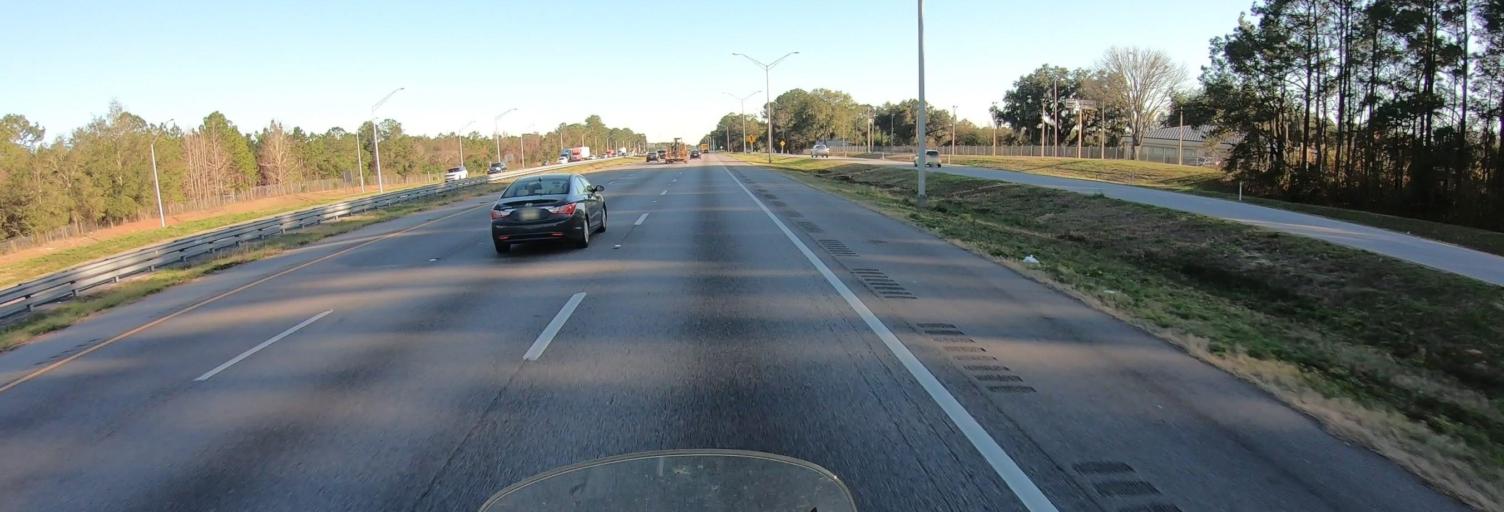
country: US
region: Florida
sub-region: Alachua County
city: Alachua
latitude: 29.6861
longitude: -82.4451
